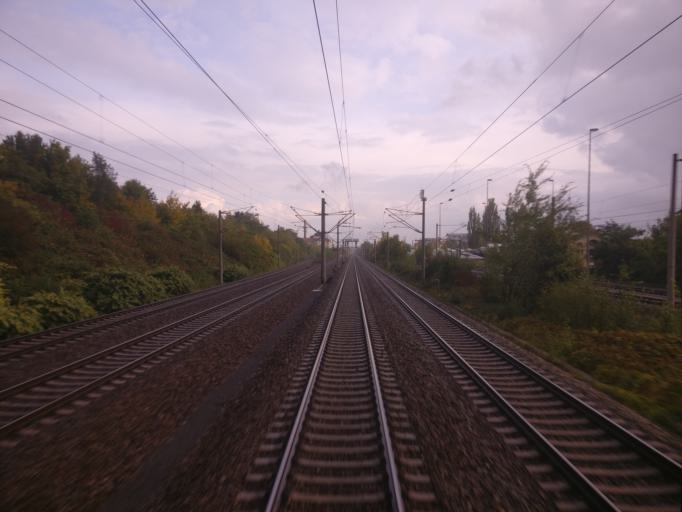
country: DE
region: Saxony
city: Heidenau
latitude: 51.0139
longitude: 13.8047
